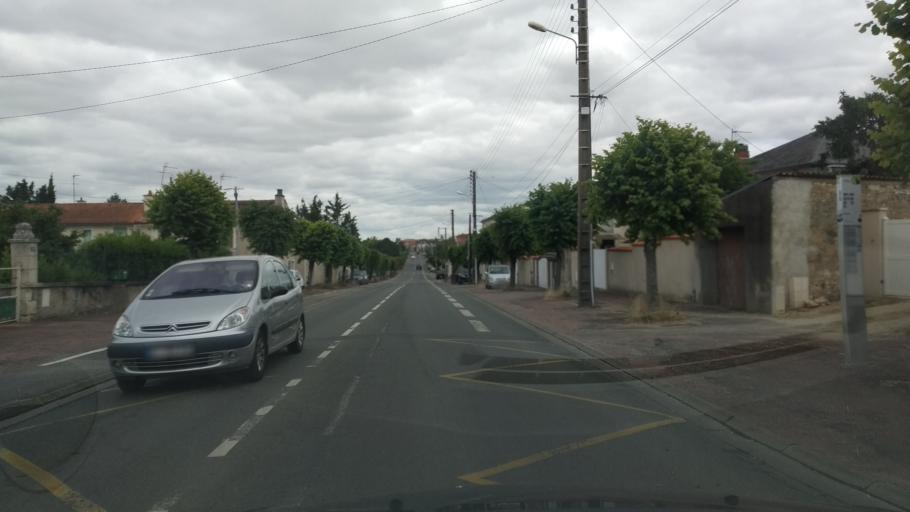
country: FR
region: Poitou-Charentes
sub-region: Departement de la Vienne
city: Poitiers
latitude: 46.5931
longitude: 0.3285
